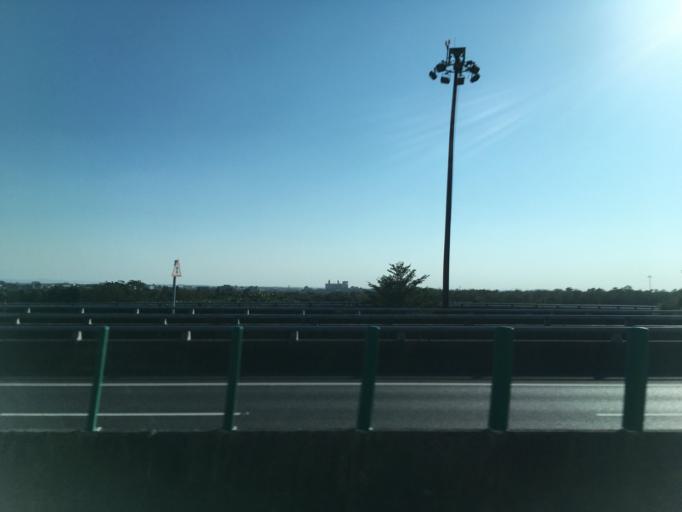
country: TW
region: Taiwan
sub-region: Chiayi
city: Taibao
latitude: 23.4241
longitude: 120.3591
